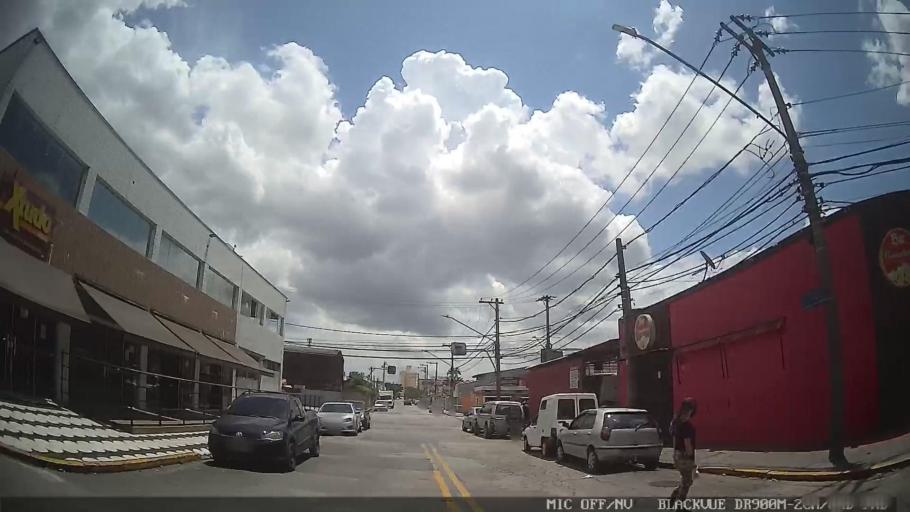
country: BR
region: Sao Paulo
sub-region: Mogi das Cruzes
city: Mogi das Cruzes
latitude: -23.5144
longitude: -46.1893
